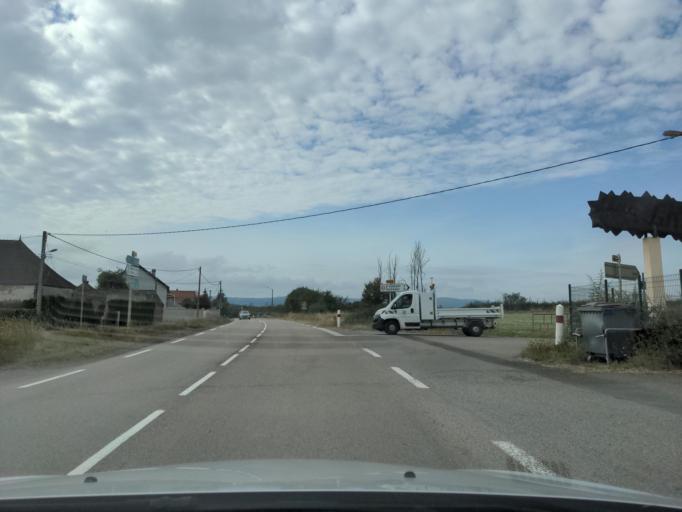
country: FR
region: Bourgogne
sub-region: Departement de Saone-et-Loire
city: Autun
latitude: 47.0100
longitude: 4.3209
